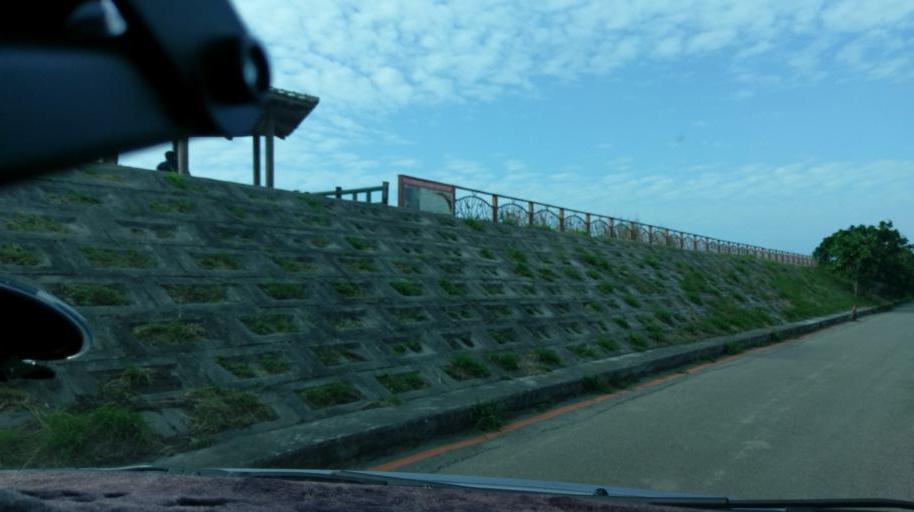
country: TW
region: Taiwan
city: Fengyuan
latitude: 24.3151
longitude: 120.5508
